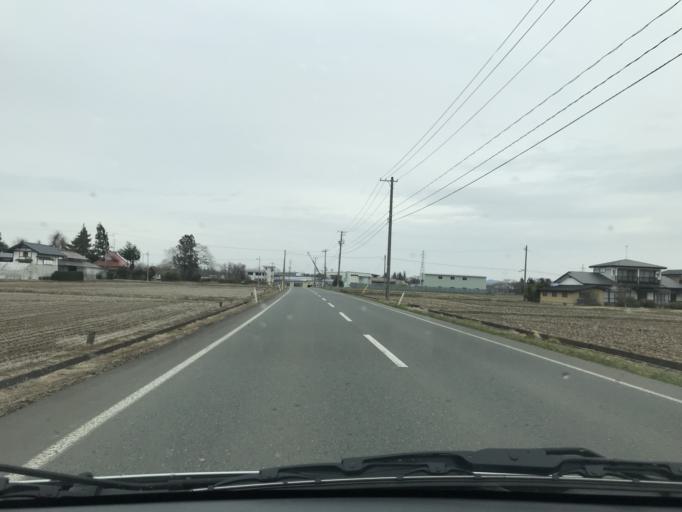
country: JP
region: Iwate
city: Mizusawa
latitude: 39.1756
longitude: 141.1135
